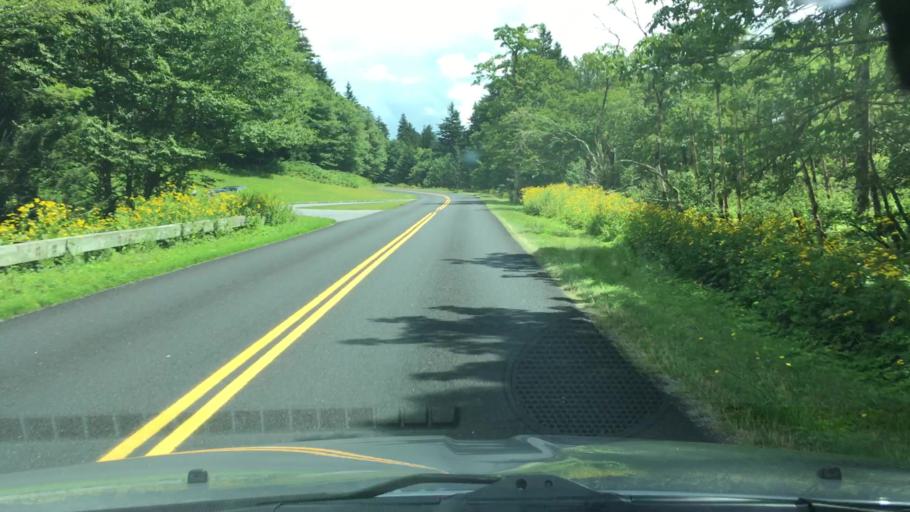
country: US
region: North Carolina
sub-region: Buncombe County
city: Black Mountain
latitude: 35.7489
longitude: -82.3343
